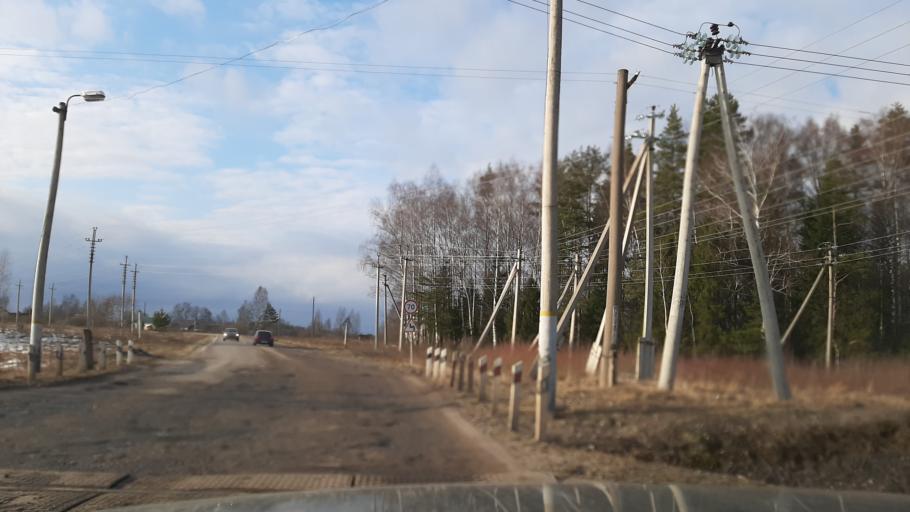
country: RU
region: Ivanovo
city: Novo-Talitsy
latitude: 56.9385
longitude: 40.7224
